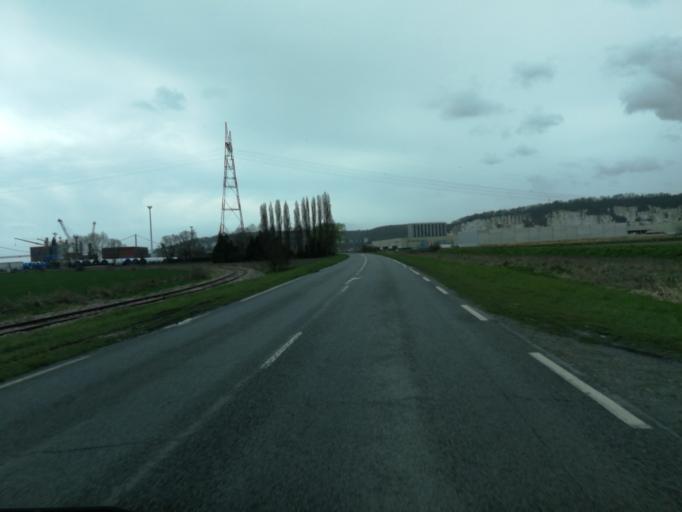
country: FR
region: Haute-Normandie
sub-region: Departement de la Seine-Maritime
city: Saint-Nicolas-de-la-Taille
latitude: 49.4891
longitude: 0.4926
